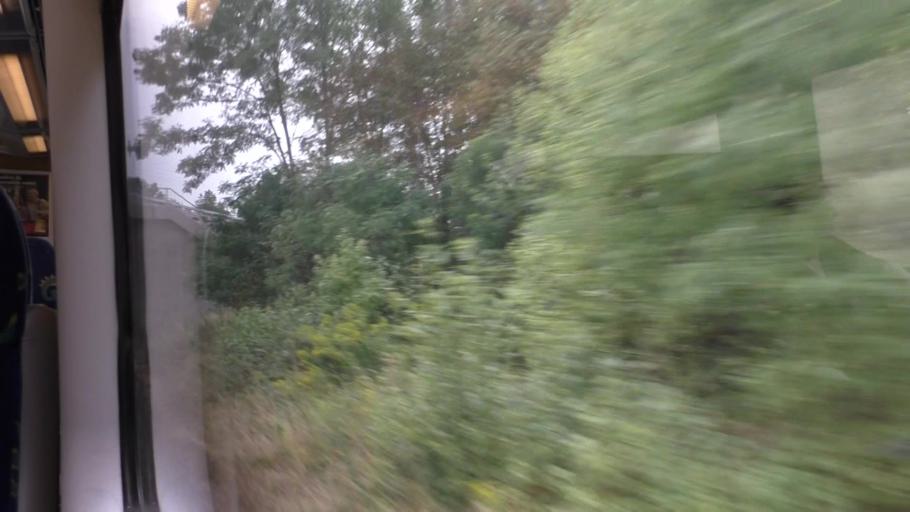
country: DE
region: Saxony
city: Ostritz
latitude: 51.0611
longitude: 14.9563
